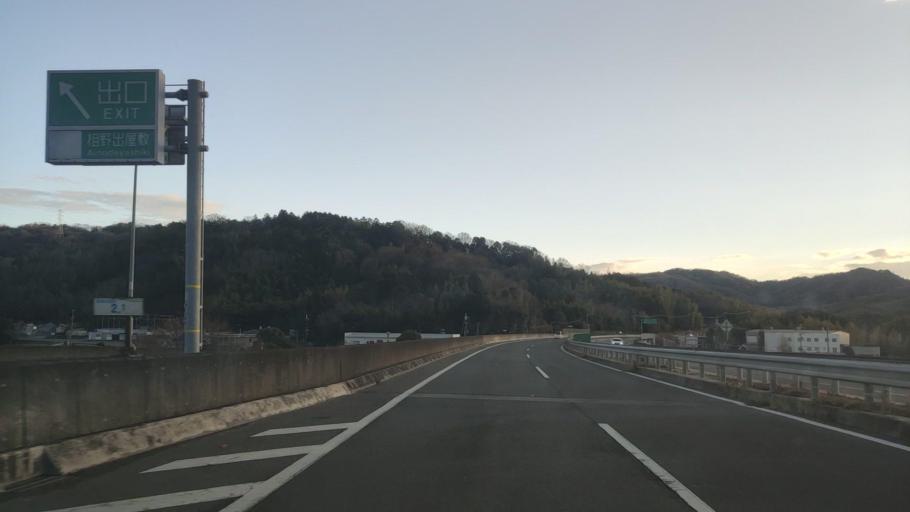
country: JP
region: Hyogo
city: Tatsunocho-tominaga
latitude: 34.8649
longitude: 134.6184
